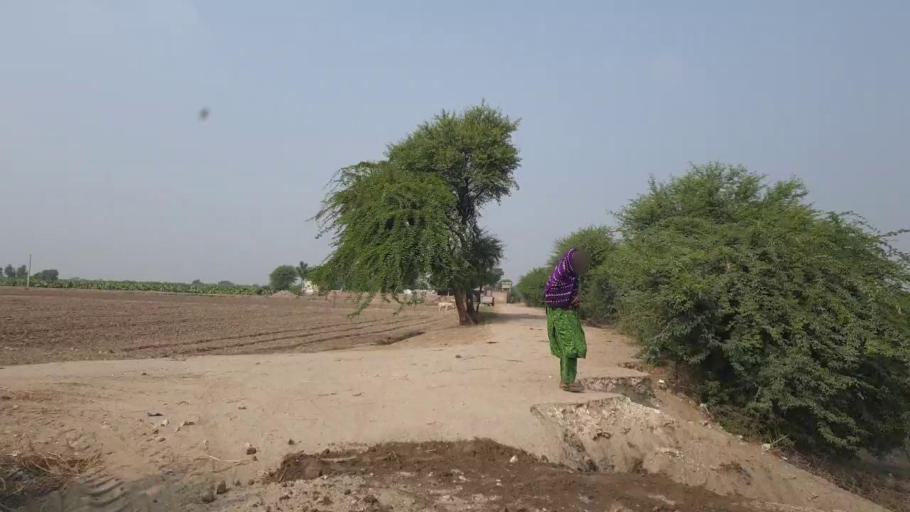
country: PK
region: Sindh
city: Matli
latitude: 25.0263
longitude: 68.5969
